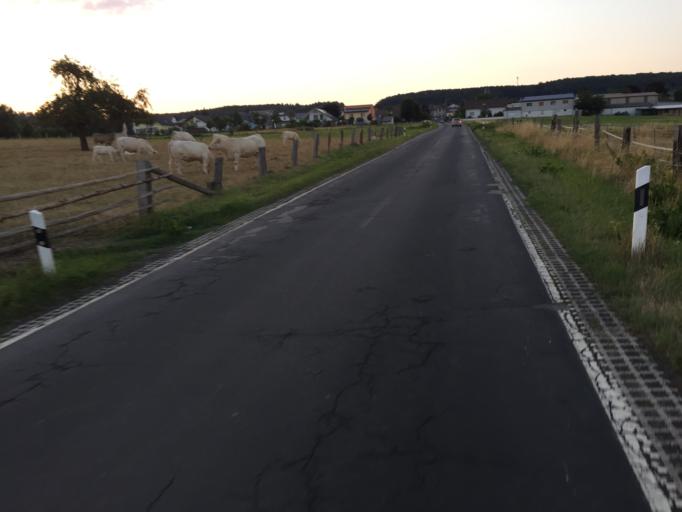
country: DE
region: Hesse
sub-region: Regierungsbezirk Giessen
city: Alten Buseck
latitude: 50.6143
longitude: 8.7528
